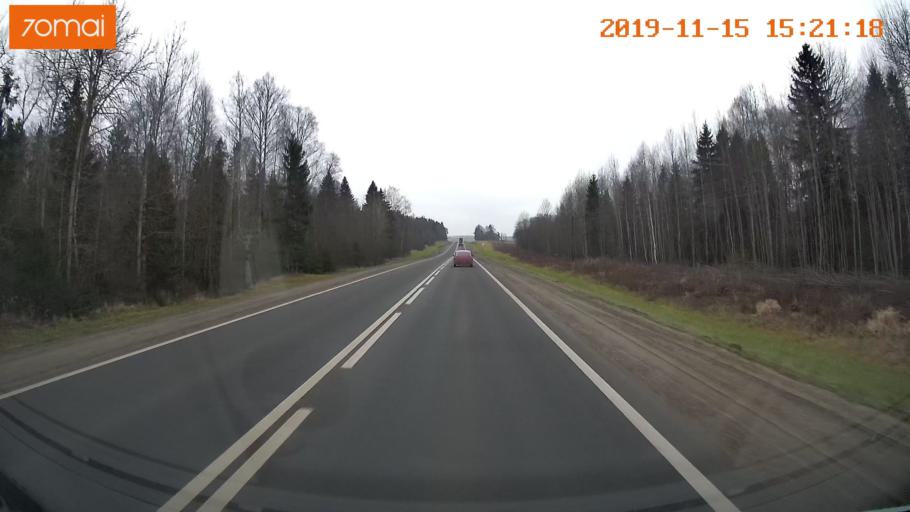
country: RU
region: Jaroslavl
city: Danilov
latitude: 58.2140
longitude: 40.1478
